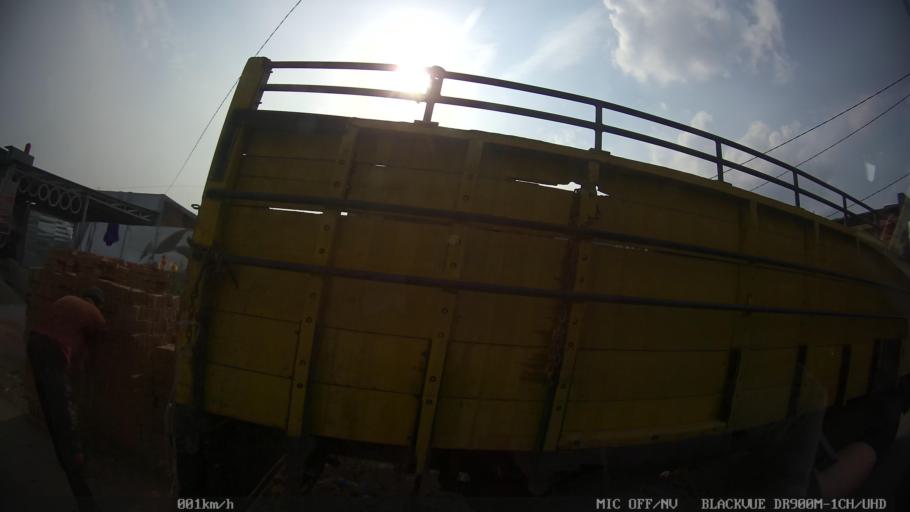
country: ID
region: North Sumatra
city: Medan
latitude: 3.5768
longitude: 98.7566
